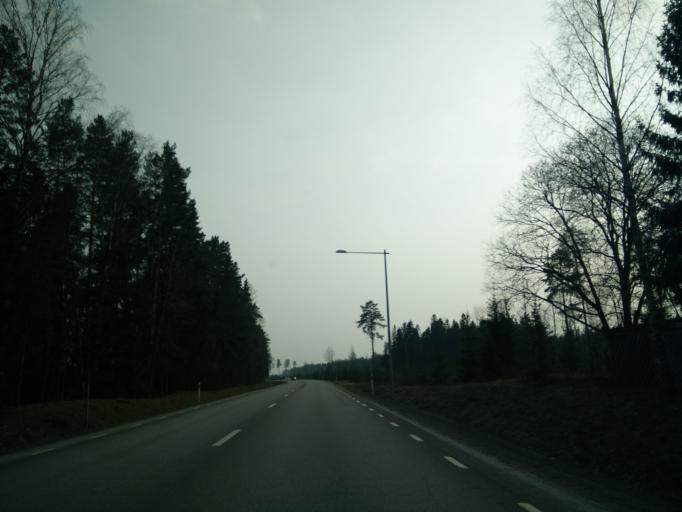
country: SE
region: Vaermland
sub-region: Forshaga Kommun
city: Forshaga
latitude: 59.5105
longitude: 13.4385
